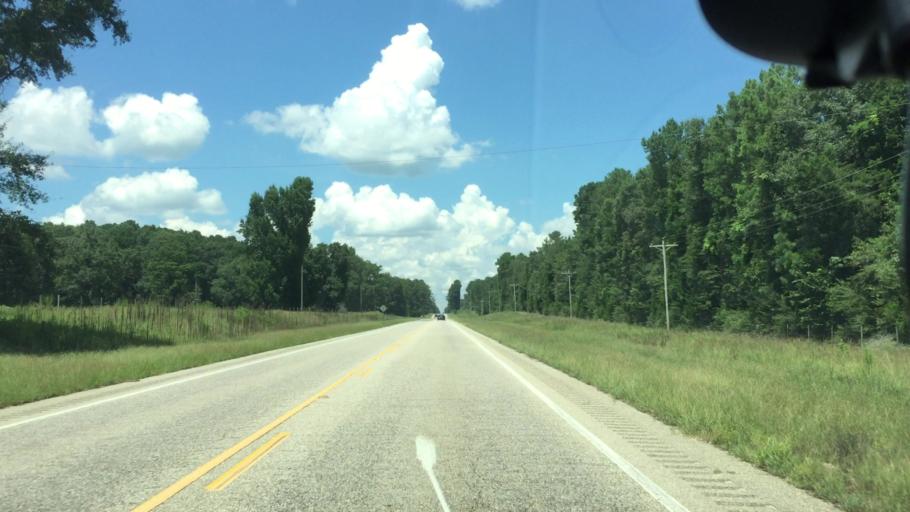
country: US
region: Alabama
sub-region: Pike County
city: Brundidge
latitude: 31.6417
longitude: -85.9473
